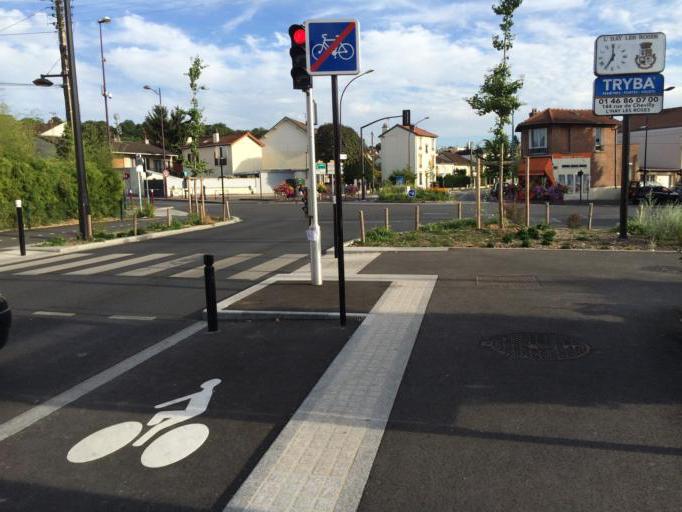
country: FR
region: Ile-de-France
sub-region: Departement du Val-de-Marne
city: L'Hay-les-Roses
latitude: 48.7798
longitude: 2.3279
